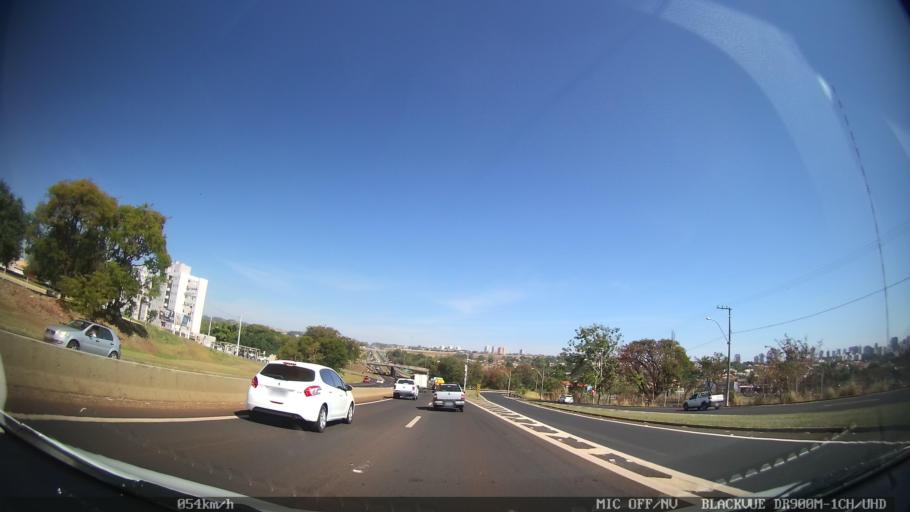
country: BR
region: Sao Paulo
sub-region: Ribeirao Preto
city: Ribeirao Preto
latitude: -21.2129
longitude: -47.7719
